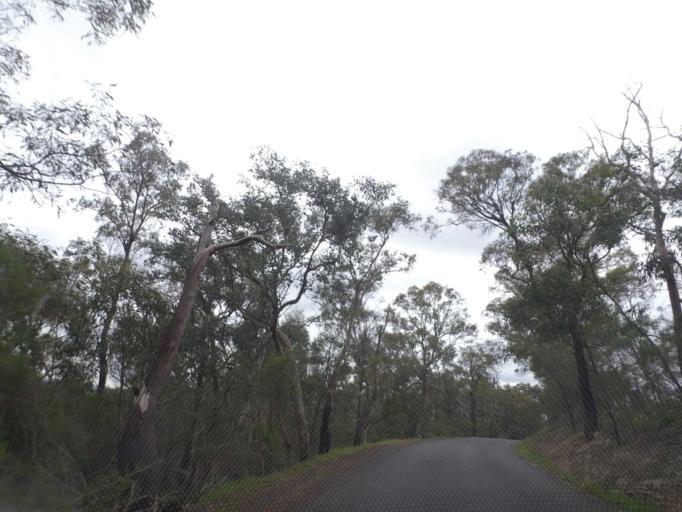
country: AU
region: Victoria
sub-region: Nillumbik
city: Hurstbridge
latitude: -37.6623
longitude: 145.2149
